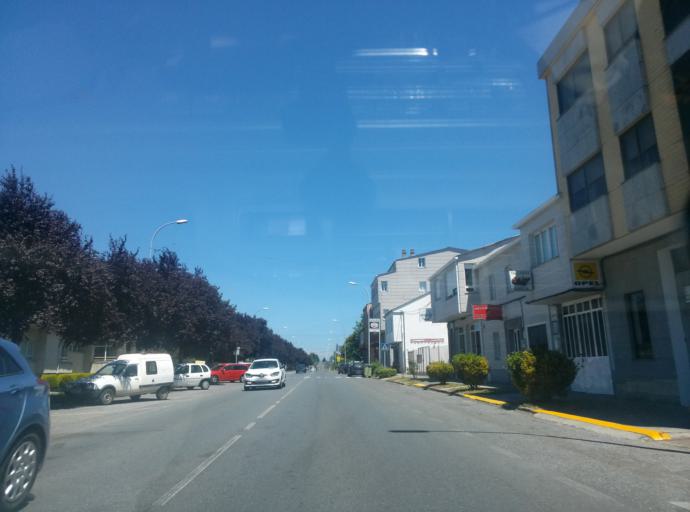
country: ES
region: Galicia
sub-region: Provincia de Lugo
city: Mos
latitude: 43.1446
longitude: -7.4917
